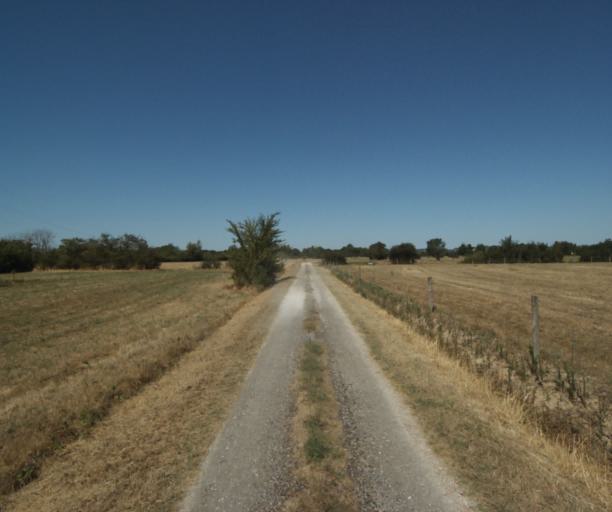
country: FR
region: Midi-Pyrenees
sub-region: Departement de la Haute-Garonne
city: Revel
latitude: 43.4686
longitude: 1.9890
